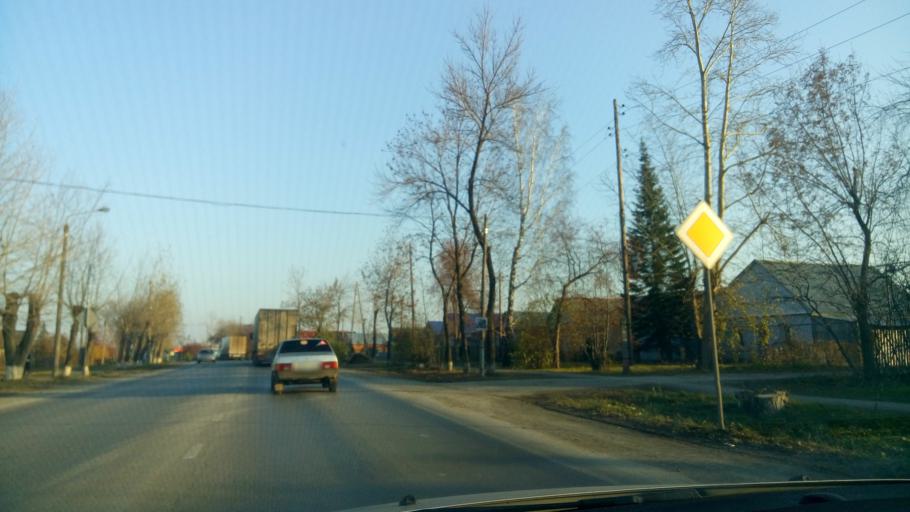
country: RU
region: Sverdlovsk
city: Bogdanovich
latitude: 56.7659
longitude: 62.0600
